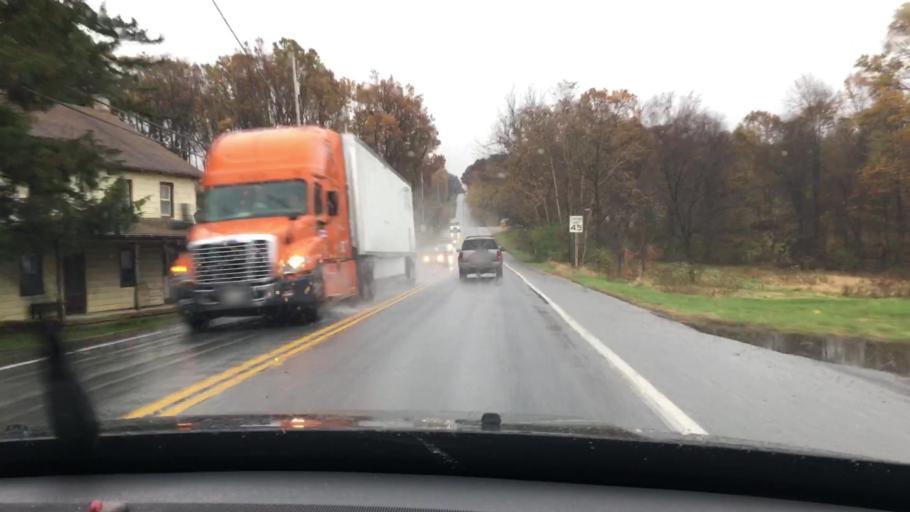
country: US
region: Pennsylvania
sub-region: Lancaster County
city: Quarryville
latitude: 39.9068
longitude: -76.2425
